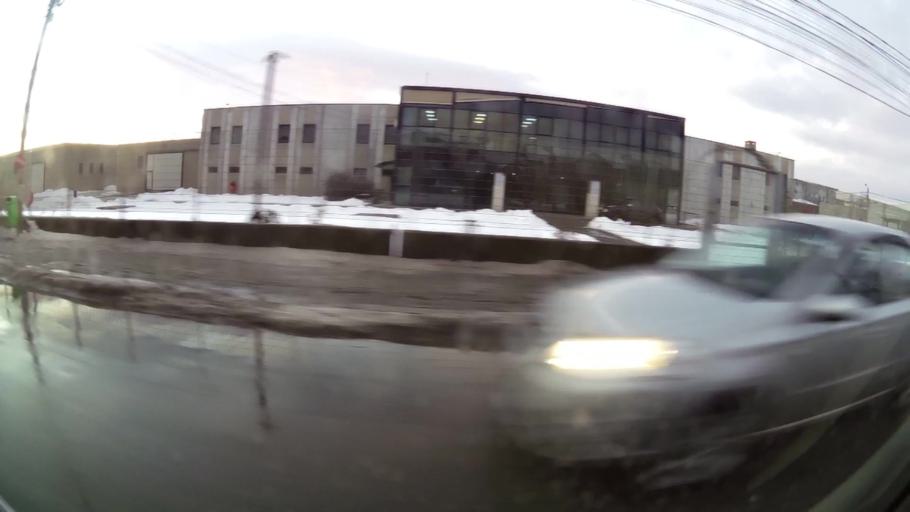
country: RO
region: Ilfov
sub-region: Comuna Popesti-Leordeni
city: Popesti-Leordeni
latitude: 44.3750
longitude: 26.1560
